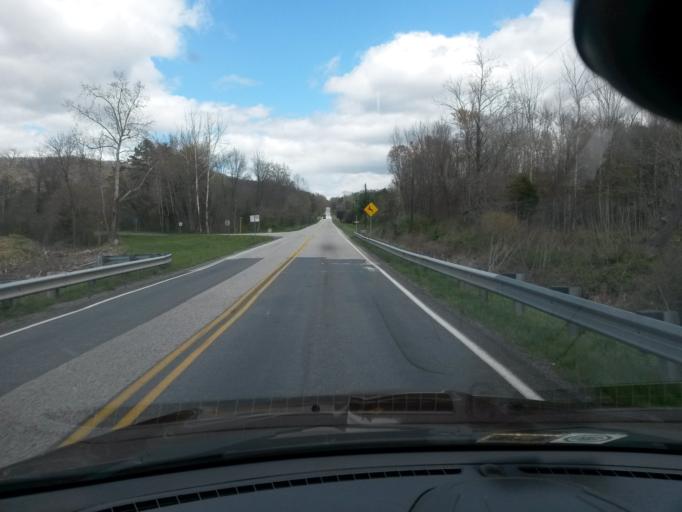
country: US
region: Virginia
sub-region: Rockbridge County
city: Glasgow
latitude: 37.6495
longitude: -79.4283
